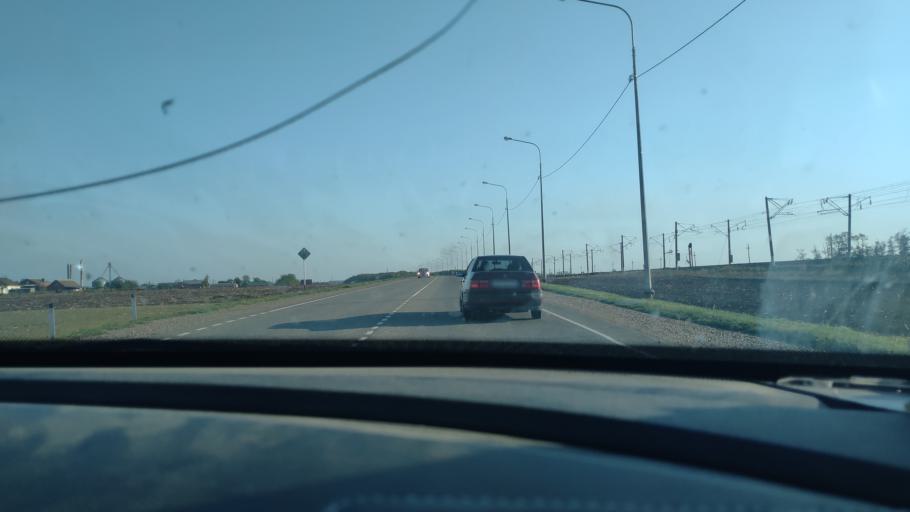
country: RU
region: Krasnodarskiy
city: Novominskaya
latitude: 46.3110
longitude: 38.9307
